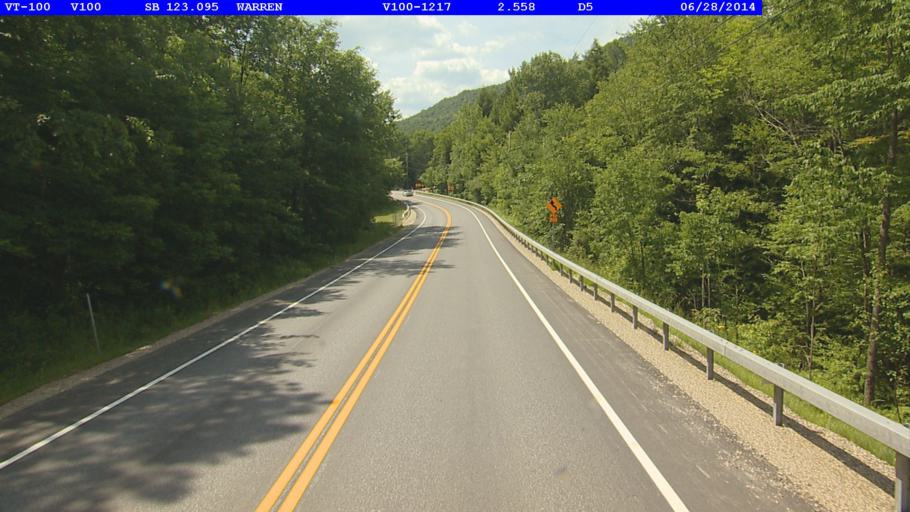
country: US
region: Vermont
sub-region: Washington County
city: Northfield
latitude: 44.0956
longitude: -72.8632
